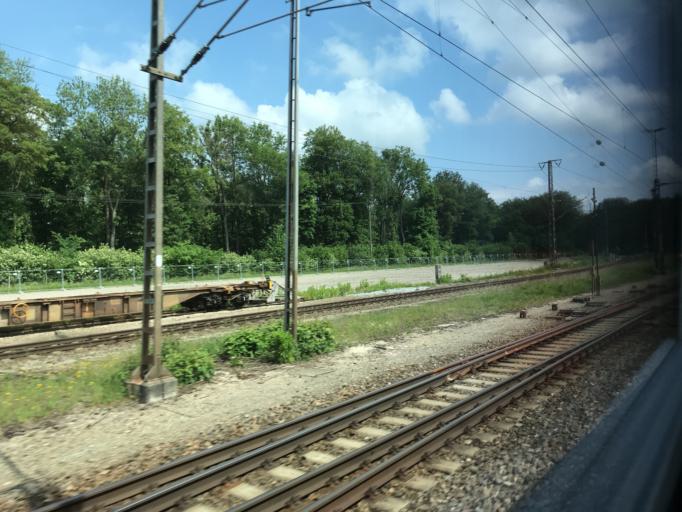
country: DE
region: Bavaria
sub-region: Swabia
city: Offingen
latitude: 48.4851
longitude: 10.3496
